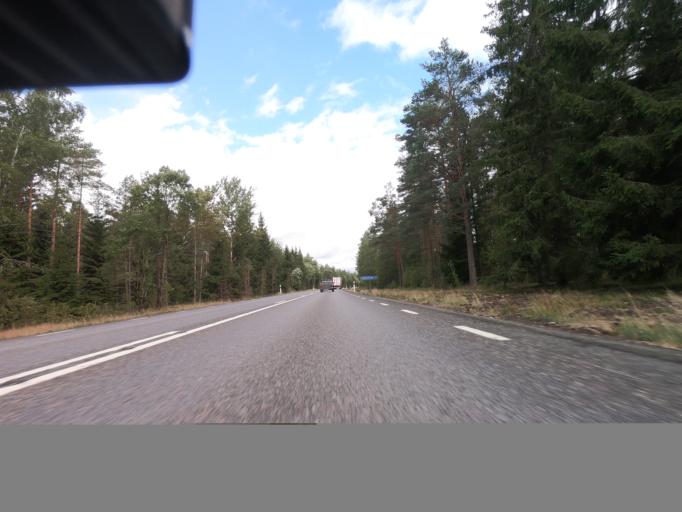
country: SE
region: Joenkoeping
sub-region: Vaggeryds Kommun
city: Vaggeryd
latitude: 57.5271
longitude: 14.2749
